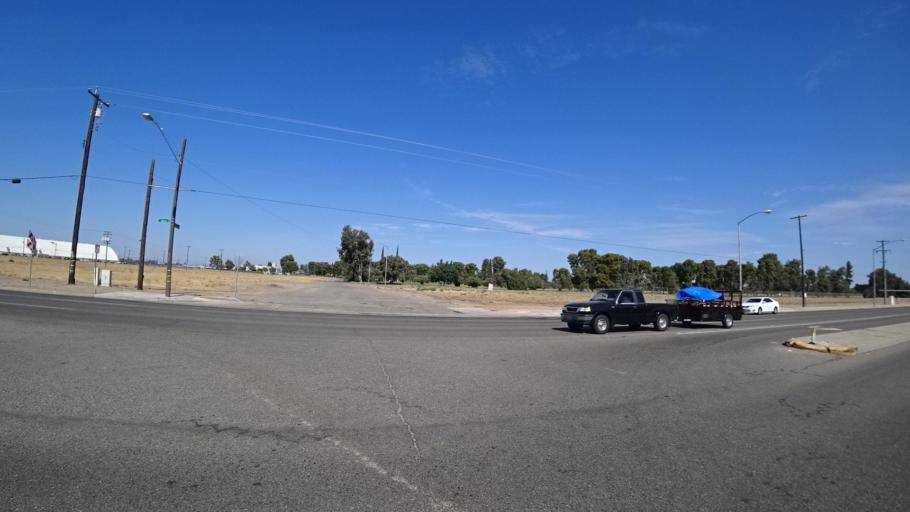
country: US
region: California
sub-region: Fresno County
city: Tarpey Village
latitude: 36.7757
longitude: -119.7002
